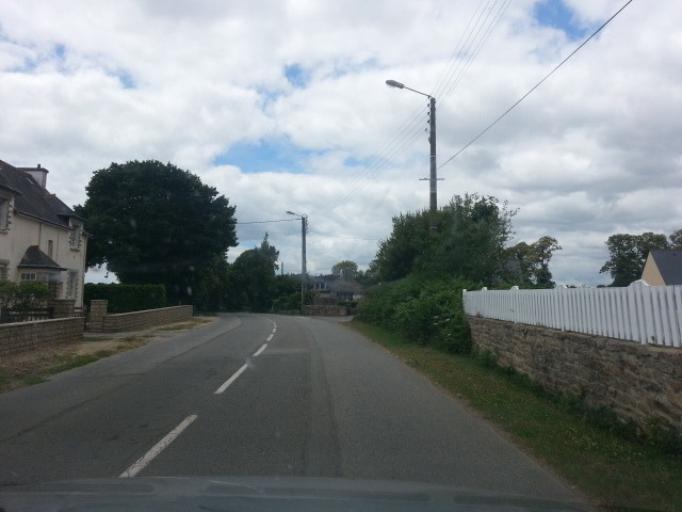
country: FR
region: Brittany
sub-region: Departement du Finistere
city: Melgven
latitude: 47.8817
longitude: -3.8379
